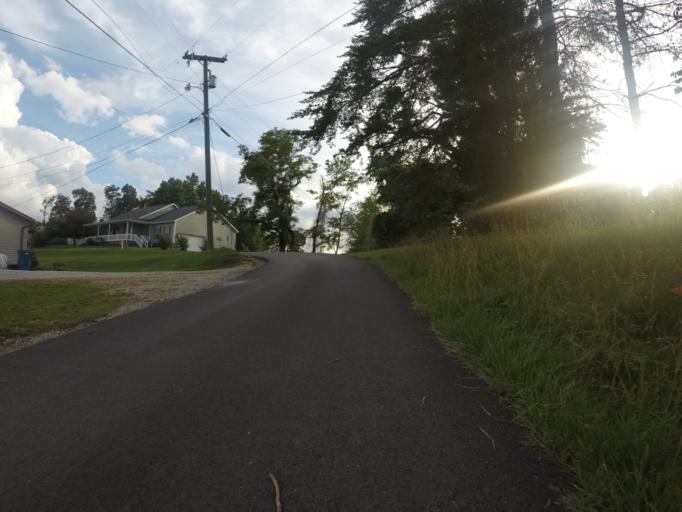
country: US
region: West Virginia
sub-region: Cabell County
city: Pea Ridge
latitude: 38.4057
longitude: -82.3583
